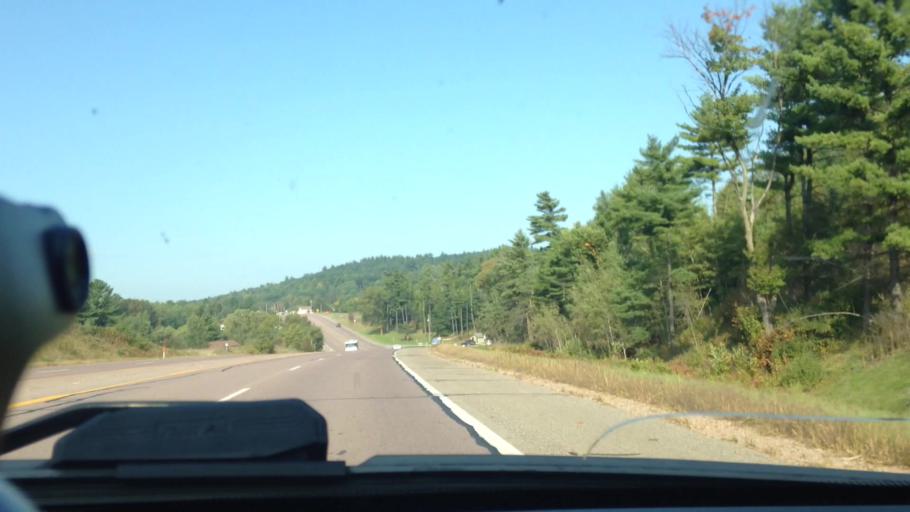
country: US
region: Michigan
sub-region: Dickinson County
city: Quinnesec
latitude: 45.8048
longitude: -87.9746
